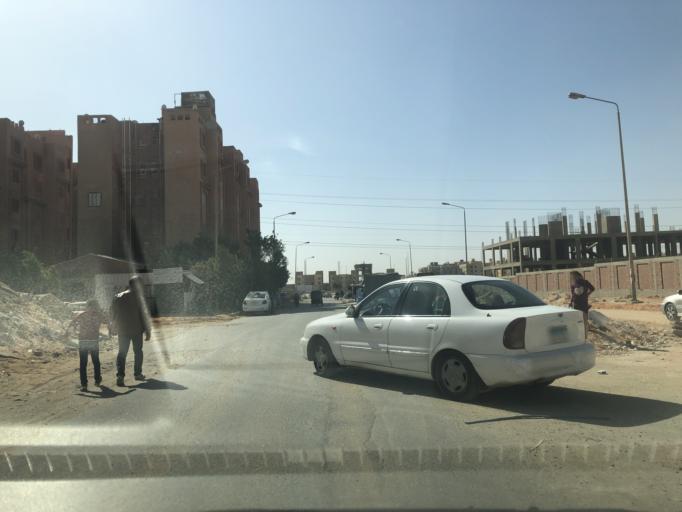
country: EG
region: Al Jizah
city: Madinat Sittah Uktubar
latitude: 29.9288
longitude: 30.9450
